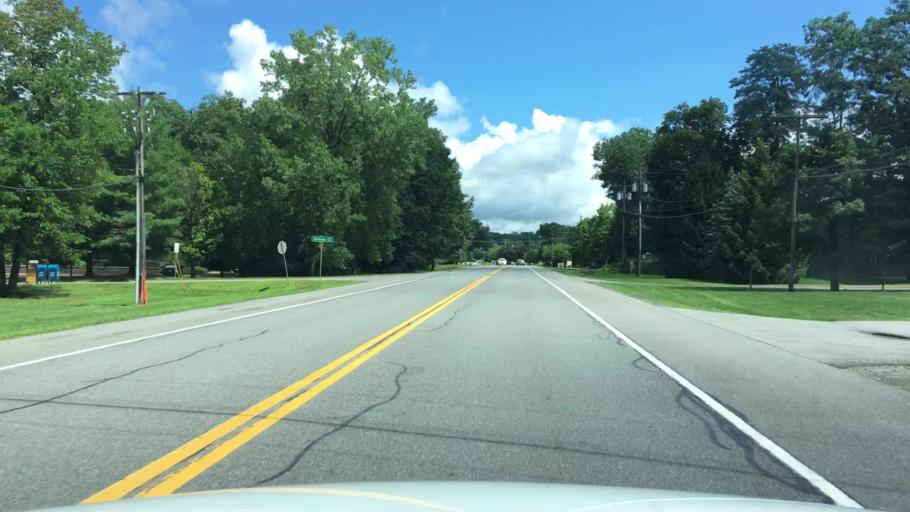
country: US
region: New York
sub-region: Albany County
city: Colonie
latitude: 42.7396
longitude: -73.8427
